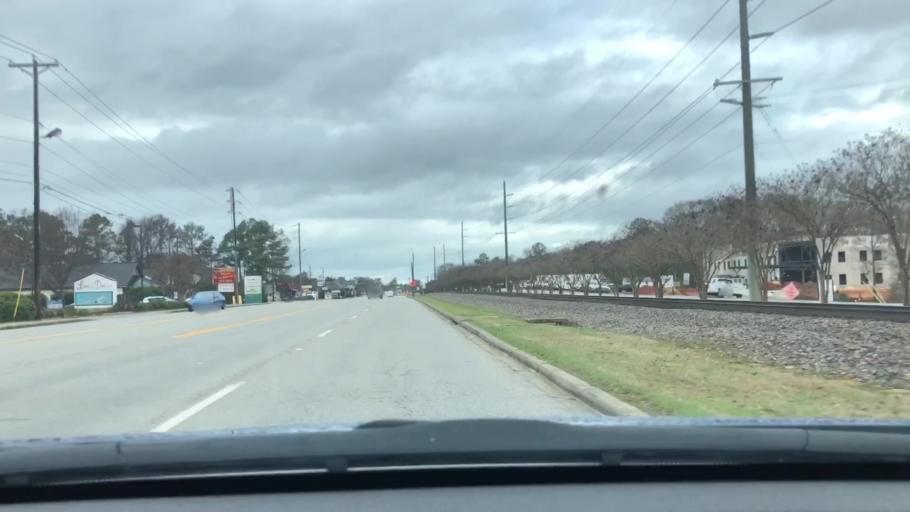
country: US
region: South Carolina
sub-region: Lexington County
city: Irmo
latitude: 34.0794
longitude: -81.1796
